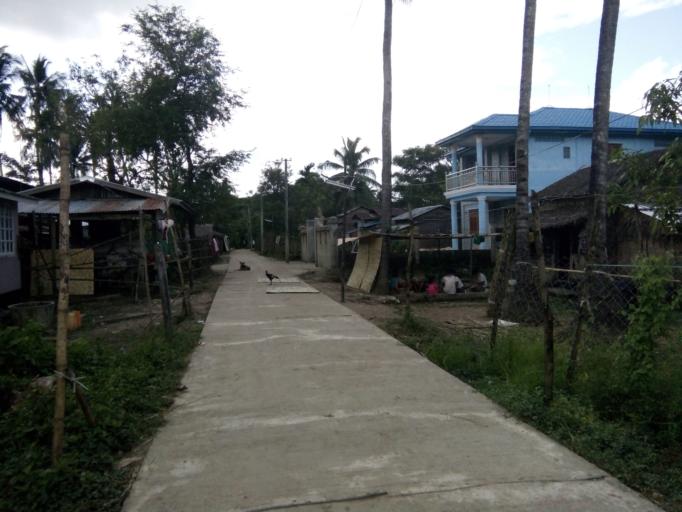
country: MM
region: Yangon
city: Kanbe
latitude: 16.8742
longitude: 95.9806
